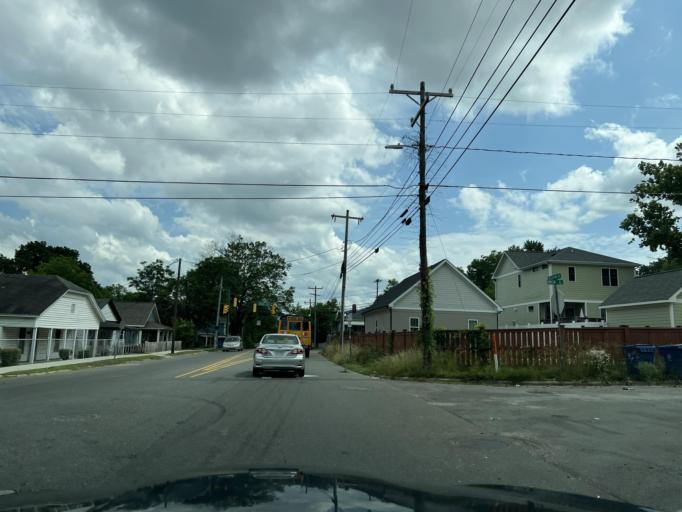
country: US
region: North Carolina
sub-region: Durham County
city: Durham
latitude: 36.0011
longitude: -78.8858
